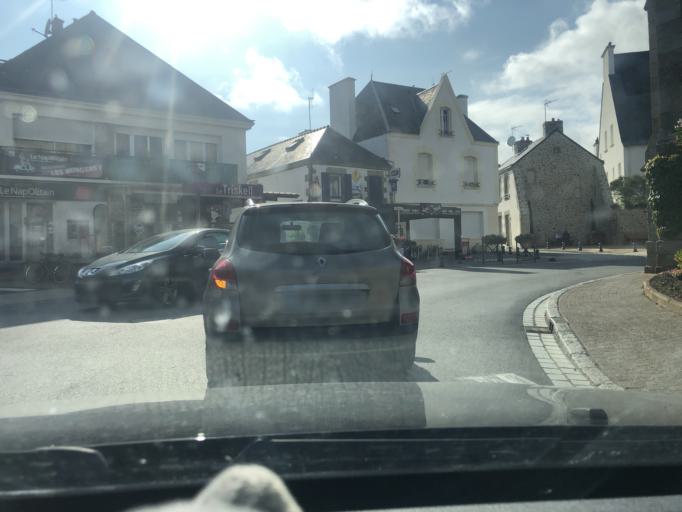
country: FR
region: Brittany
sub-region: Departement du Morbihan
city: Merlevenez
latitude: 47.6971
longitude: -3.2512
